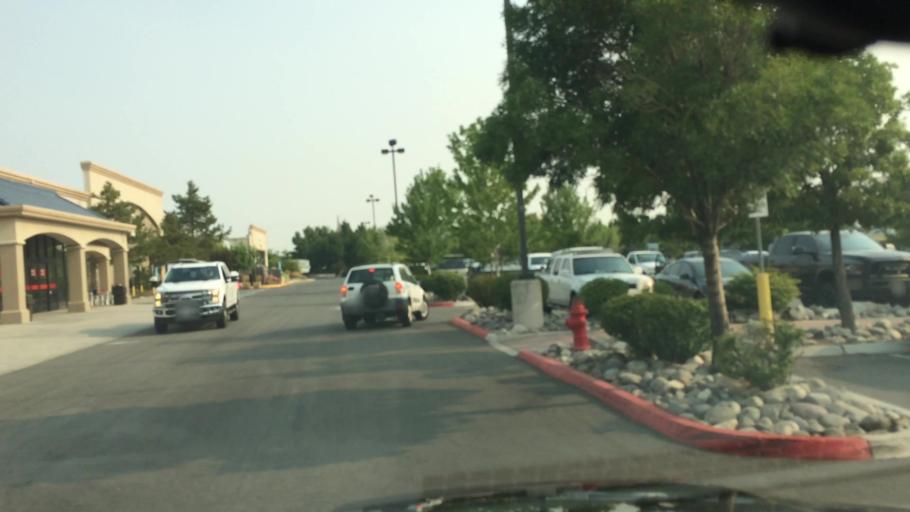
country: US
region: Nevada
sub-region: Washoe County
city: Reno
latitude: 39.4747
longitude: -119.7944
